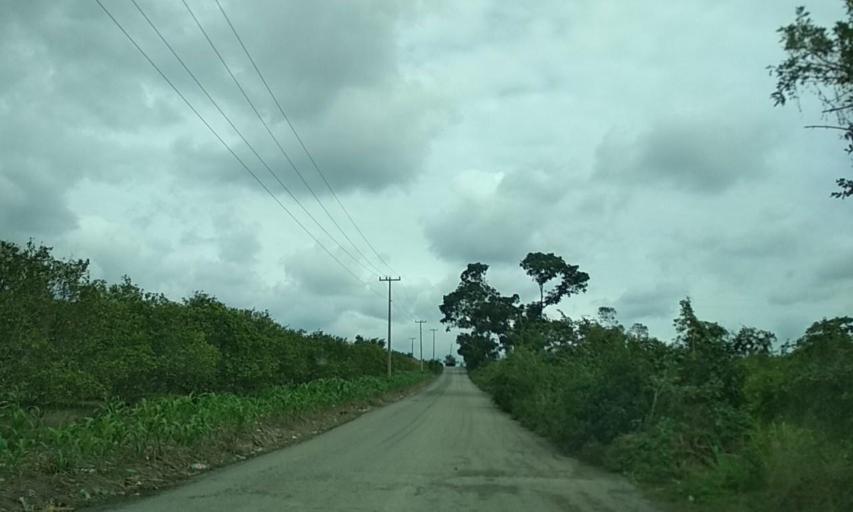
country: MX
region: Veracruz
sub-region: Papantla
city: El Chote
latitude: 20.3552
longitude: -97.3468
